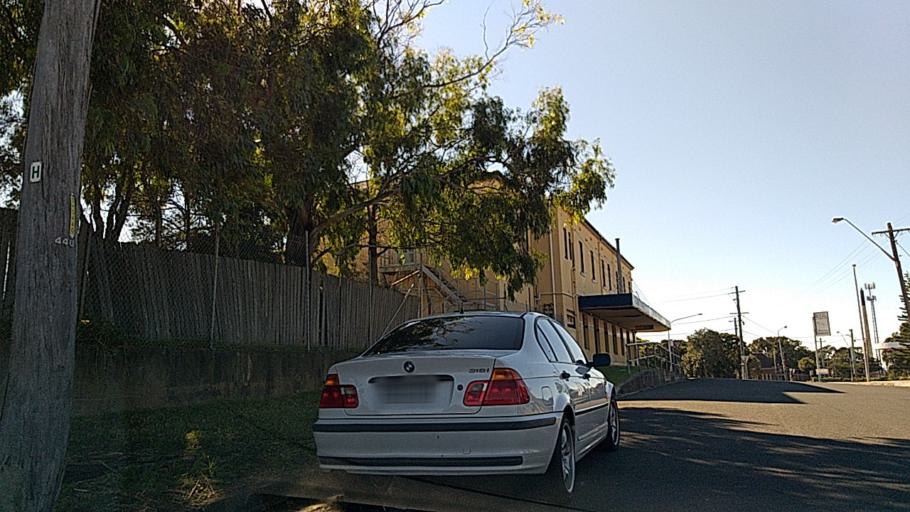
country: AU
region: New South Wales
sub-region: Wollongong
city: Port Kembla
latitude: -34.4803
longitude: 150.8999
